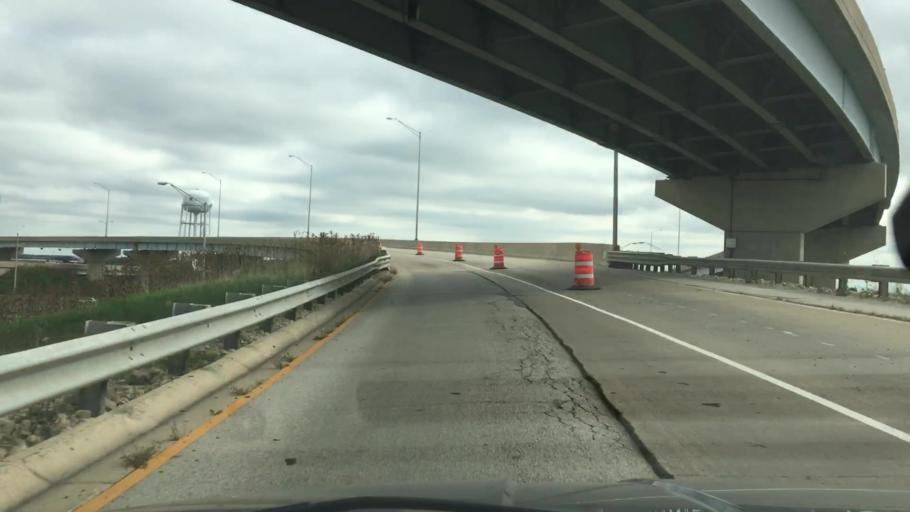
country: US
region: Illinois
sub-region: Will County
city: Bolingbrook
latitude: 41.7051
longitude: -88.0333
